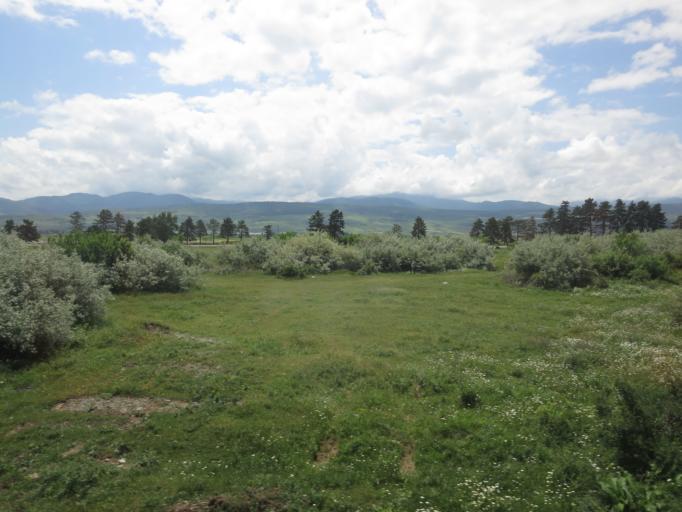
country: GE
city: Agara
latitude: 42.0273
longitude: 43.7623
